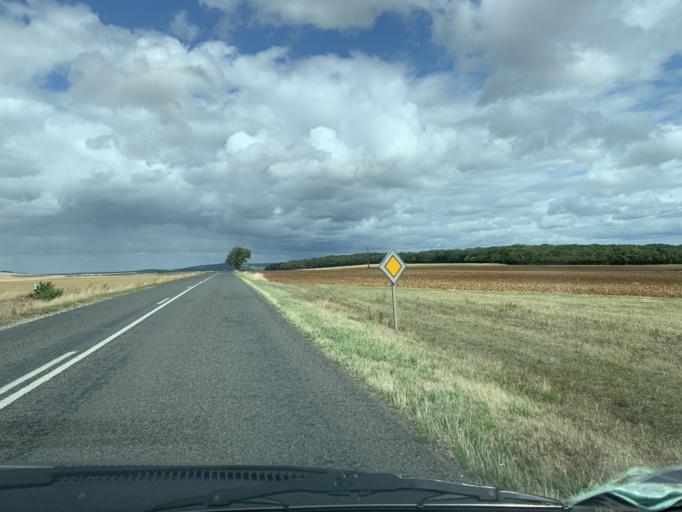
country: FR
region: Bourgogne
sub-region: Departement de la Nievre
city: Clamecy
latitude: 47.4211
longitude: 3.4669
